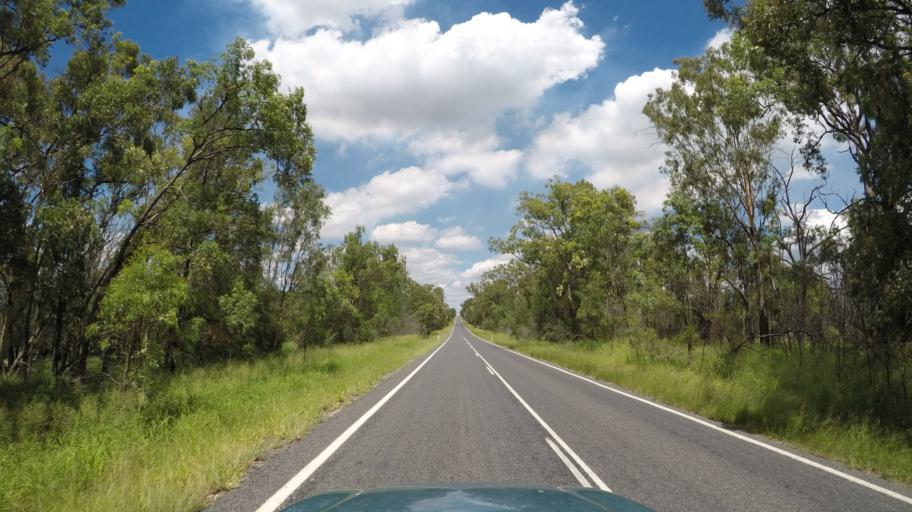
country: AU
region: Queensland
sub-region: Toowoomba
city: Oakey
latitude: -27.9358
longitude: 151.1668
